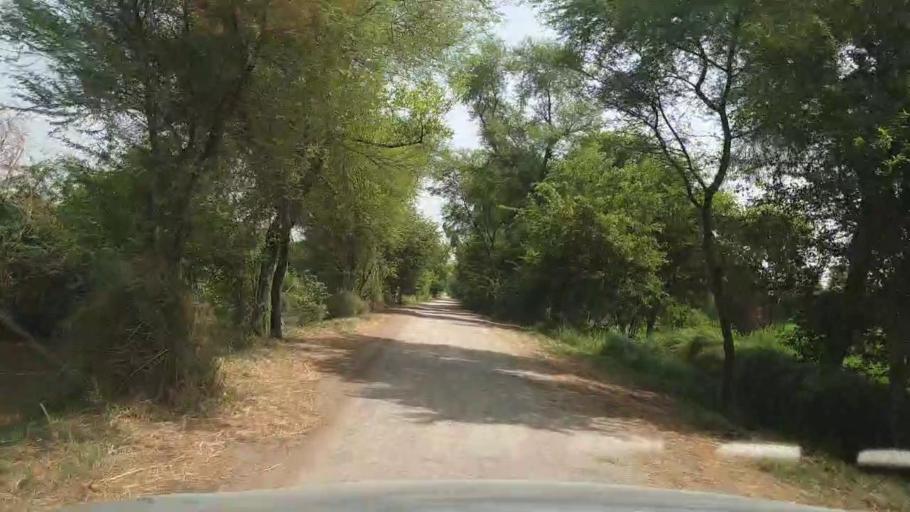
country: PK
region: Sindh
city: Garhi Yasin
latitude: 27.9497
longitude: 68.3779
